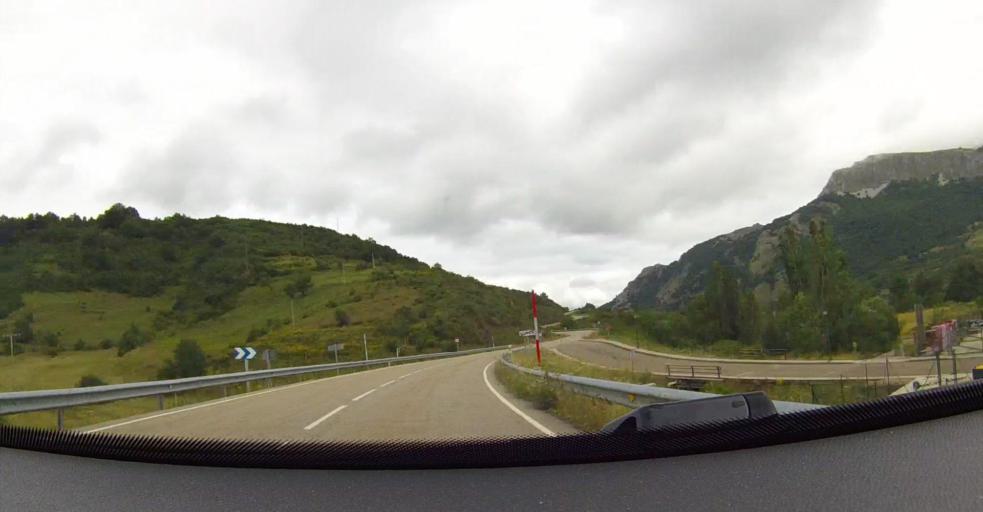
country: ES
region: Castille and Leon
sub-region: Provincia de Leon
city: Buron
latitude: 43.0250
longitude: -5.0472
